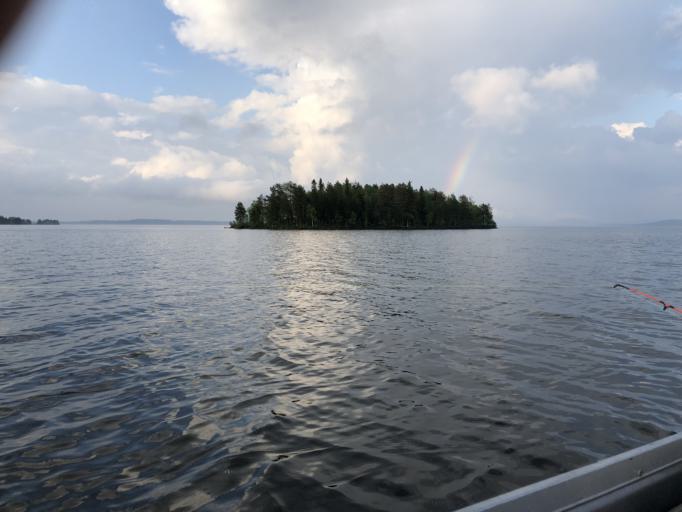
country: FI
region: Lapland
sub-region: Itae-Lappi
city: Posio
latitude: 66.1263
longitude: 28.5252
